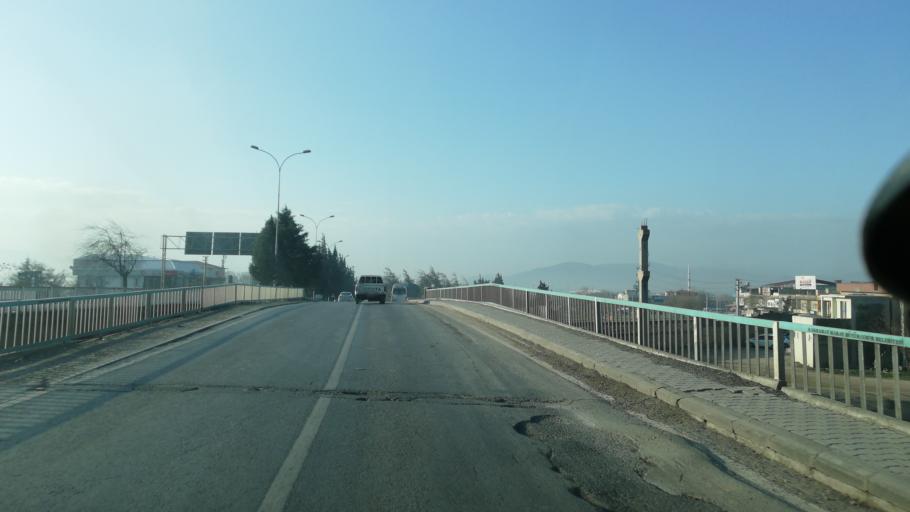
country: TR
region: Kahramanmaras
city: Kahramanmaras
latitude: 37.5664
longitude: 36.9243
